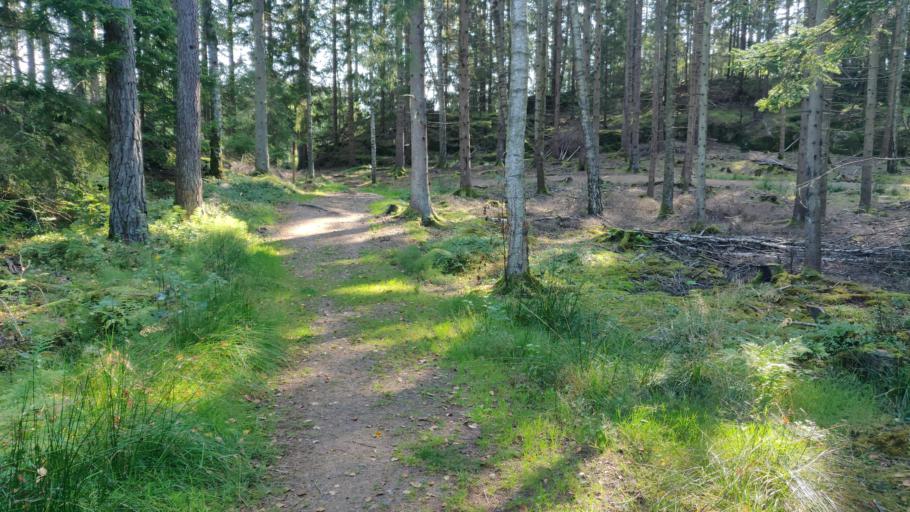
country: SE
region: Vaestra Goetaland
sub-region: Munkedals Kommun
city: Munkedal
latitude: 58.4152
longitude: 11.6151
